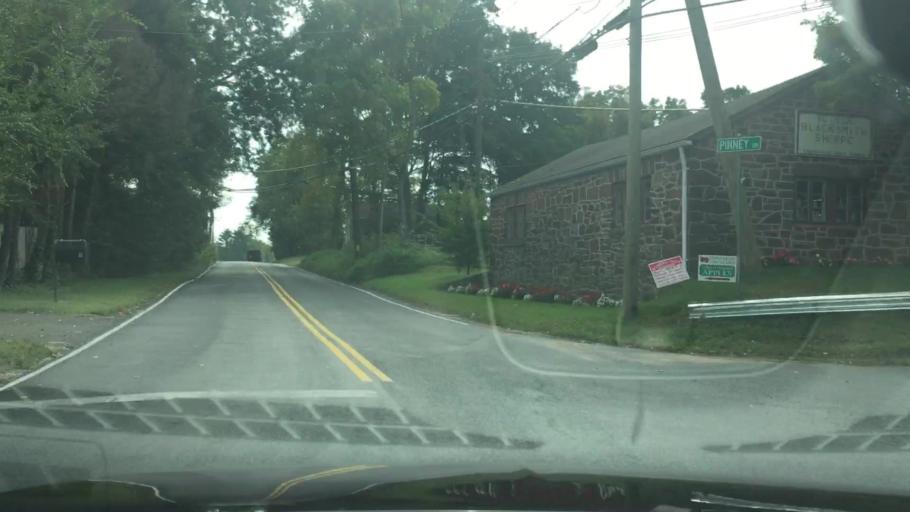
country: US
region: Connecticut
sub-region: Tolland County
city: Somers
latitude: 41.9809
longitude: -72.4880
